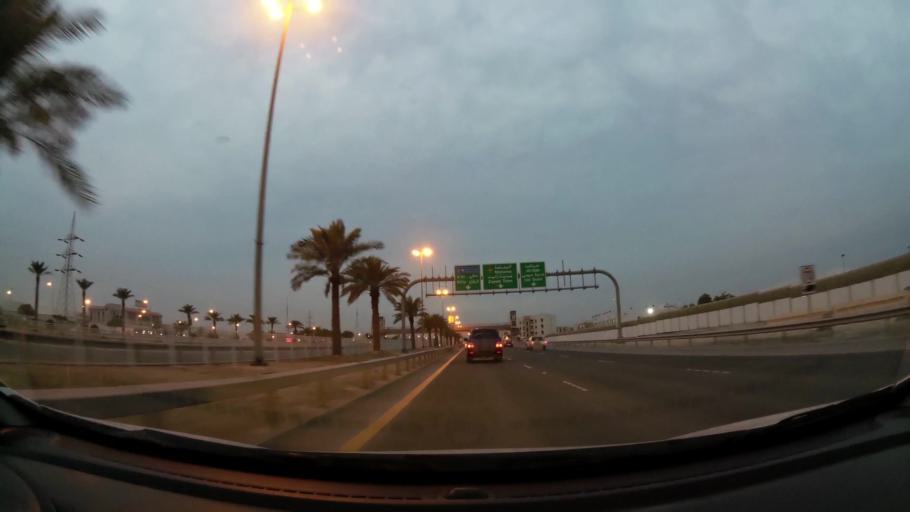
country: BH
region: Northern
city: Madinat `Isa
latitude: 26.1577
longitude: 50.5668
